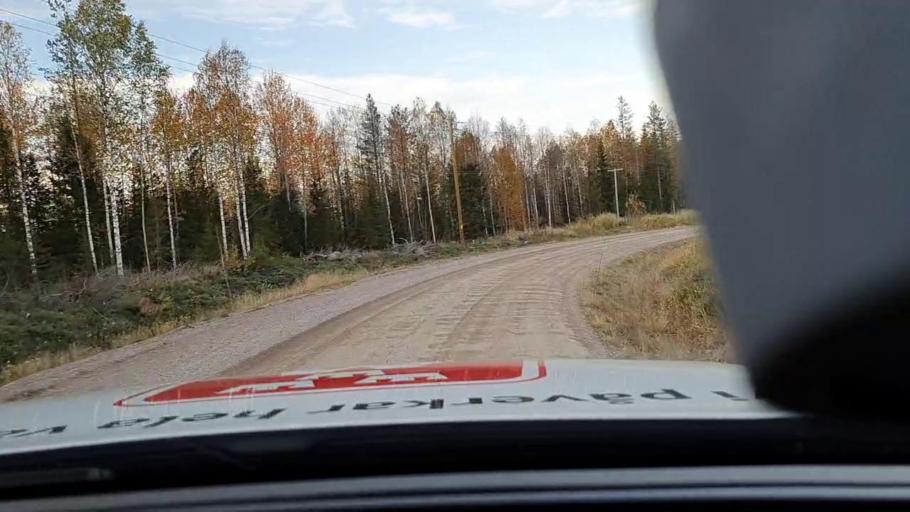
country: SE
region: Norrbotten
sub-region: Overkalix Kommun
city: OEverkalix
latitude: 66.3272
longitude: 22.5449
